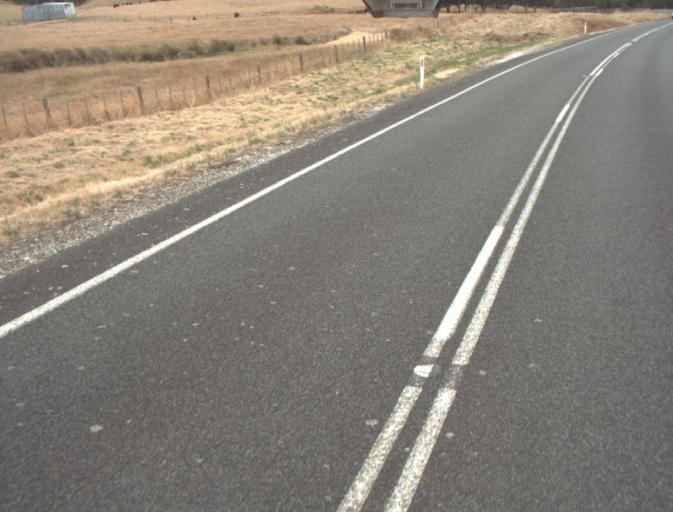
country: AU
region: Tasmania
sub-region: Launceston
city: Mayfield
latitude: -41.2826
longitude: 147.2188
